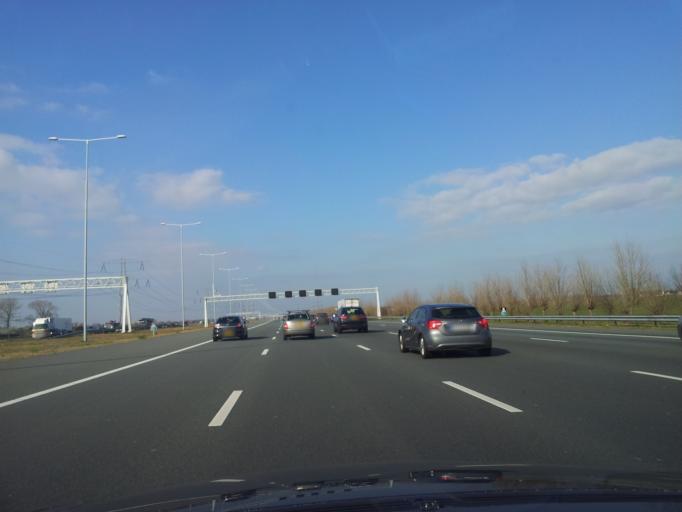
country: NL
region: Utrecht
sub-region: Stichtse Vecht
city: Breukelen
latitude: 52.1953
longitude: 4.9870
